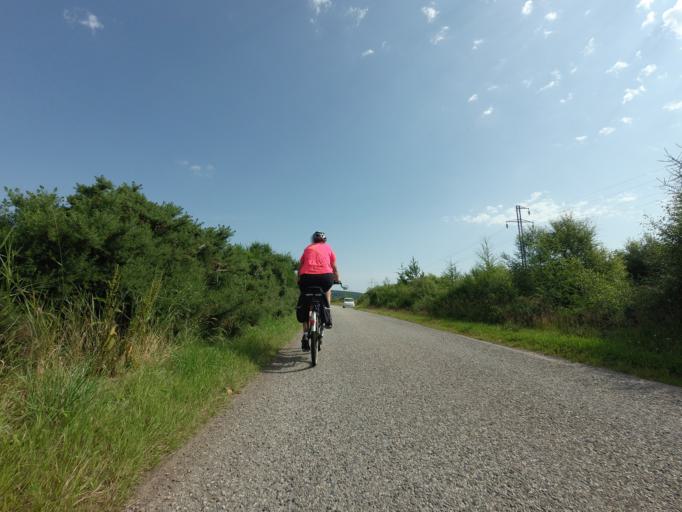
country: GB
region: Scotland
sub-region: Highland
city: Invergordon
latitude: 57.7421
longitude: -4.1786
